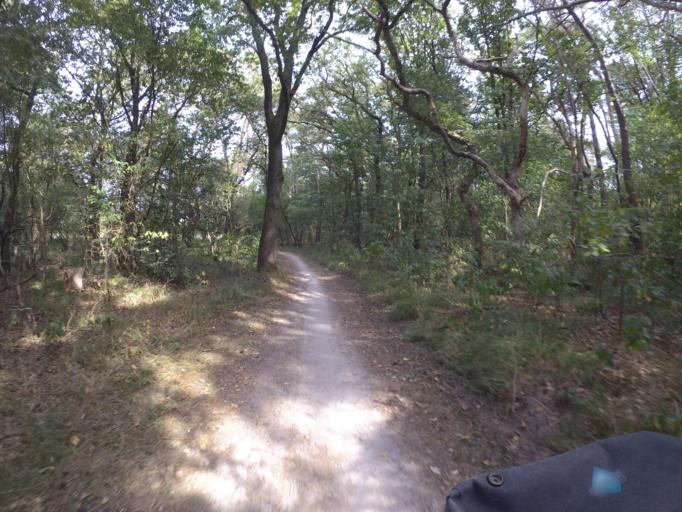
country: NL
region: Drenthe
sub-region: Gemeente Westerveld
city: Havelte
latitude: 52.8194
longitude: 6.2739
